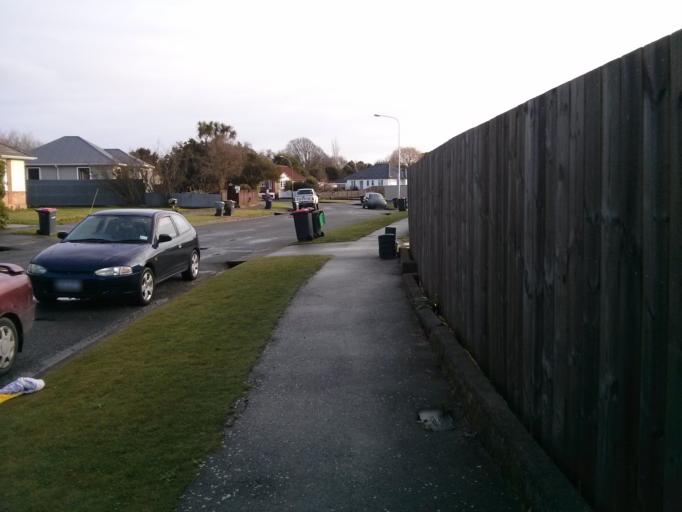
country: NZ
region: Canterbury
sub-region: Christchurch City
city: Christchurch
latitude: -43.5334
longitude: 172.5909
